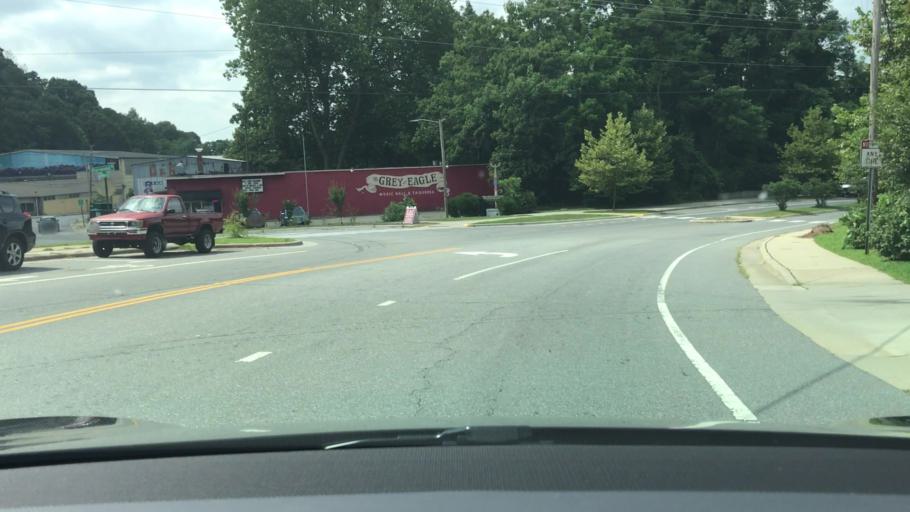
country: US
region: North Carolina
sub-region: Buncombe County
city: Asheville
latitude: 35.5879
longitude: -82.5642
